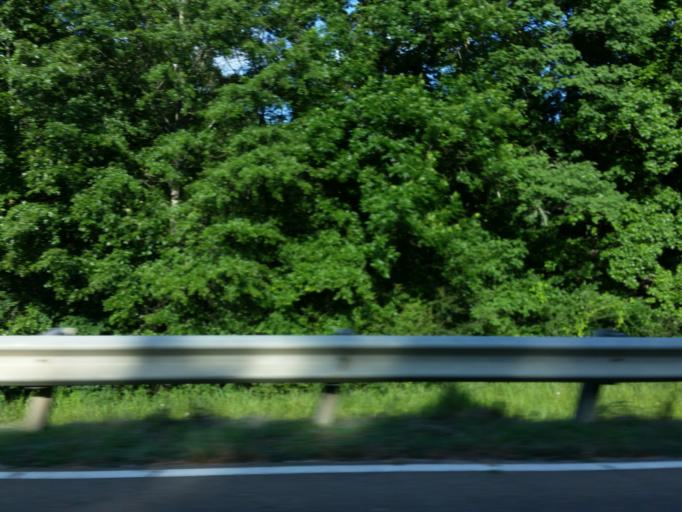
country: US
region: Mississippi
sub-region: Calhoun County
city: Calhoun City
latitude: 33.7749
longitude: -89.3640
